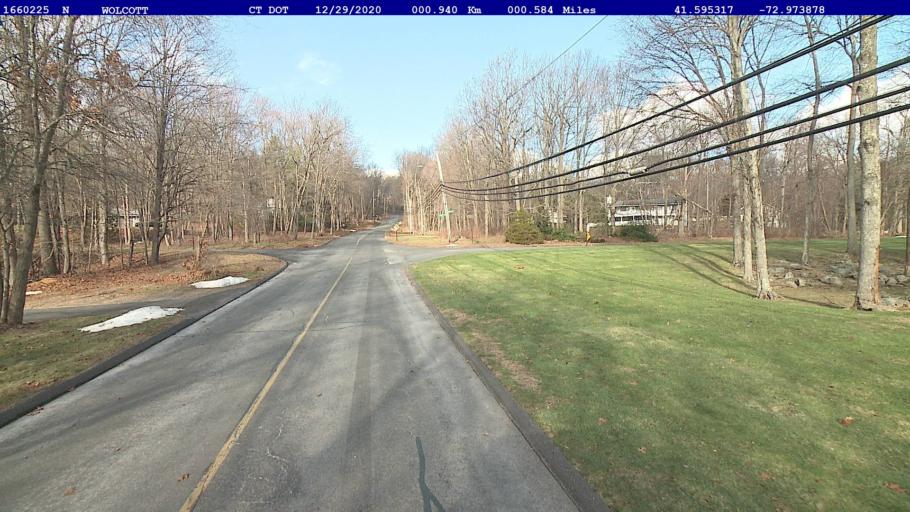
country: US
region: Connecticut
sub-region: New Haven County
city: Wolcott
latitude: 41.5953
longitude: -72.9739
